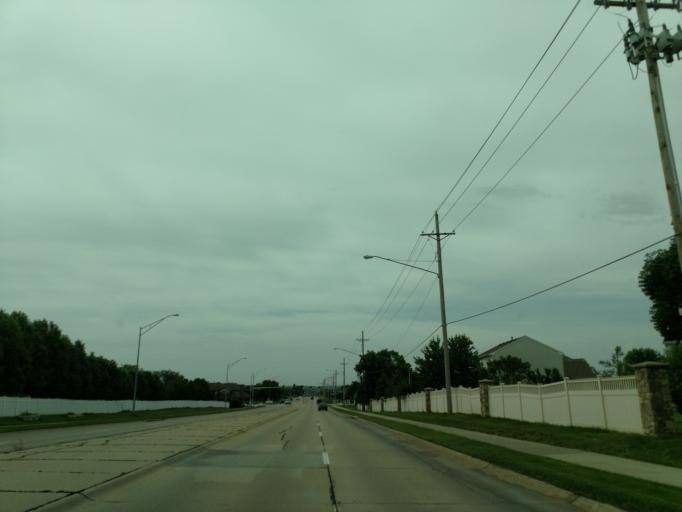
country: US
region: Nebraska
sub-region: Douglas County
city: Ralston
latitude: 41.1819
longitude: -96.0621
